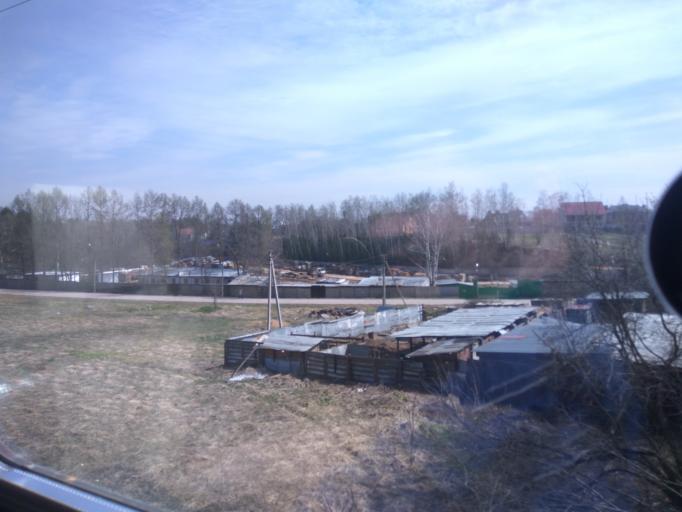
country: RU
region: Moskovskaya
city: Yermolino
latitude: 56.1285
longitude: 37.5197
